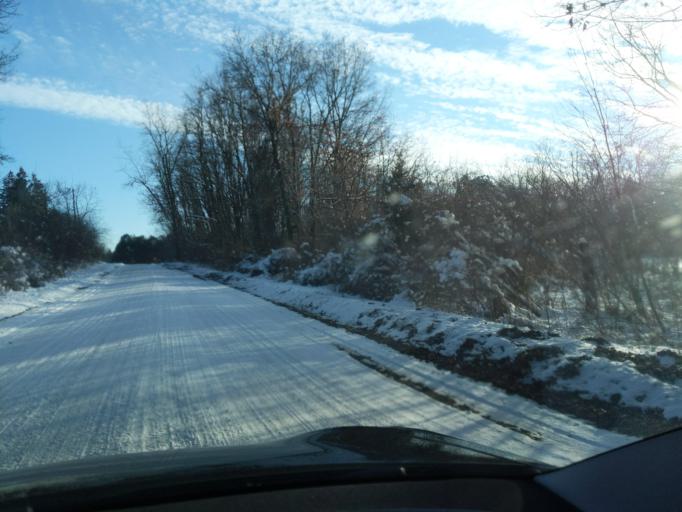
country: US
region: Michigan
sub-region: Ingham County
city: Stockbridge
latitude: 42.4333
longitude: -84.0762
